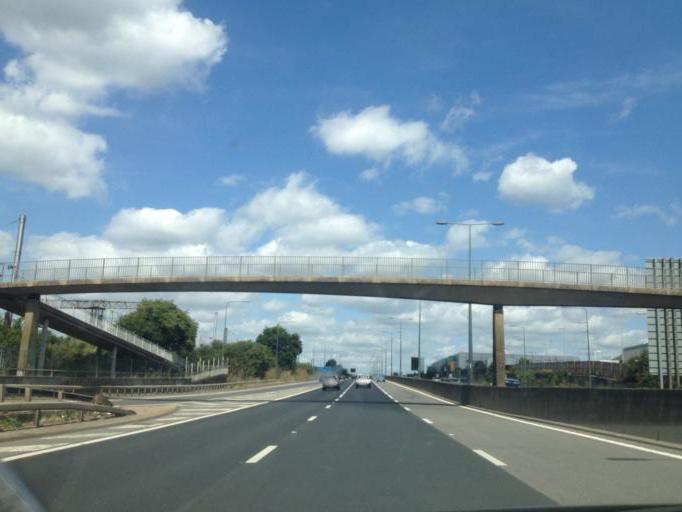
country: GB
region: England
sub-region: Greater London
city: Hendon
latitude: 51.6046
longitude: -0.2404
